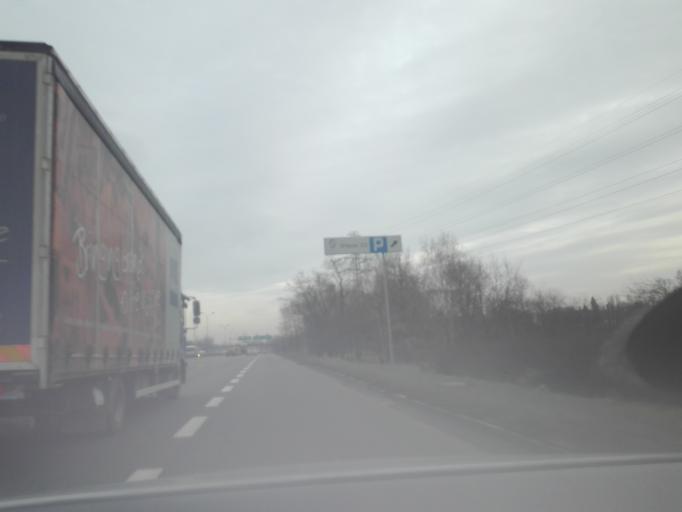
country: PL
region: Silesian Voivodeship
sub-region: Chorzow
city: Chorzow
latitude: 50.2710
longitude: 18.9772
